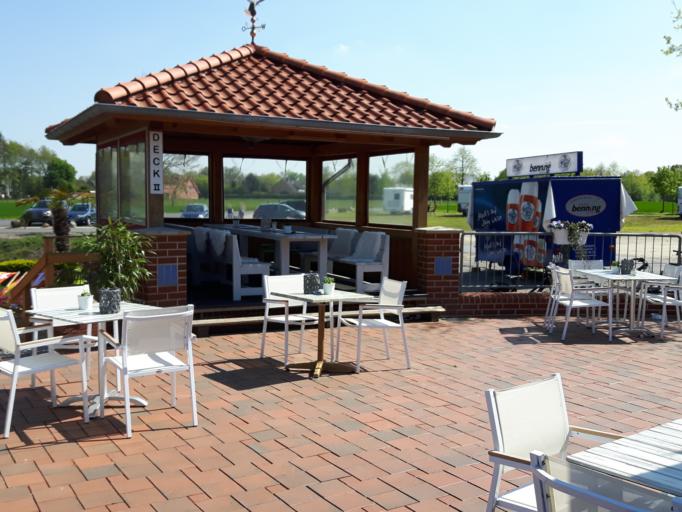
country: DE
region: North Rhine-Westphalia
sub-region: Regierungsbezirk Munster
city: Recke
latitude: 52.3533
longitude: 7.7115
